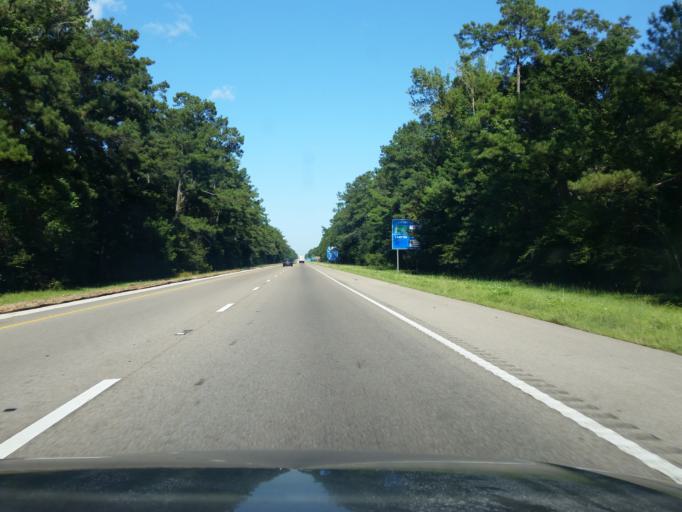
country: US
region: Mississippi
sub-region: Hancock County
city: Pearlington
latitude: 30.3098
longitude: -89.6164
